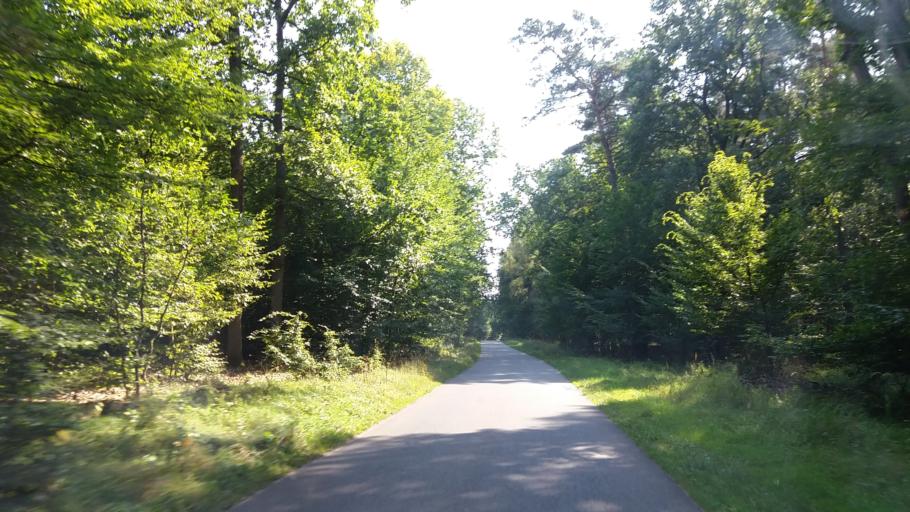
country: PL
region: West Pomeranian Voivodeship
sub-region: Powiat walecki
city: Czlopa
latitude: 53.1031
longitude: 15.9280
